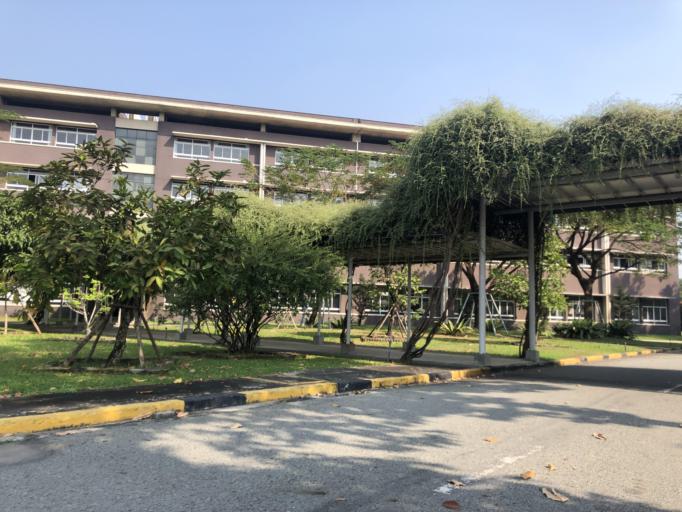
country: VN
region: Binh Duong
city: Thu Dau Mot
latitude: 11.0535
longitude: 106.6667
